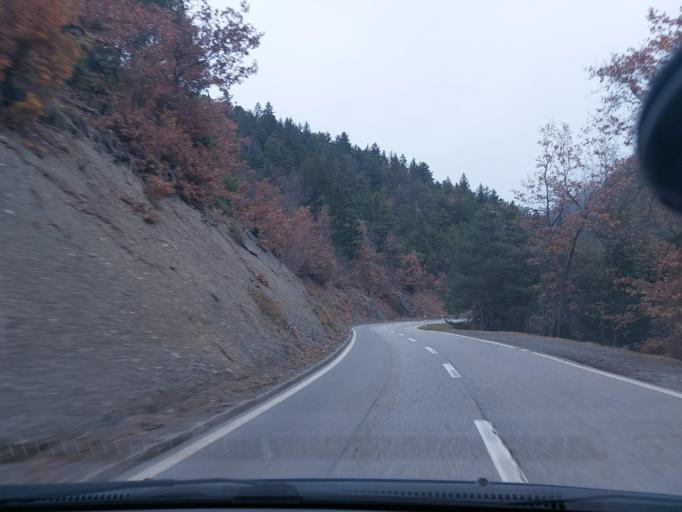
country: CH
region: Valais
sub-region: Herens District
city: Ayent
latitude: 46.2940
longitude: 7.4286
